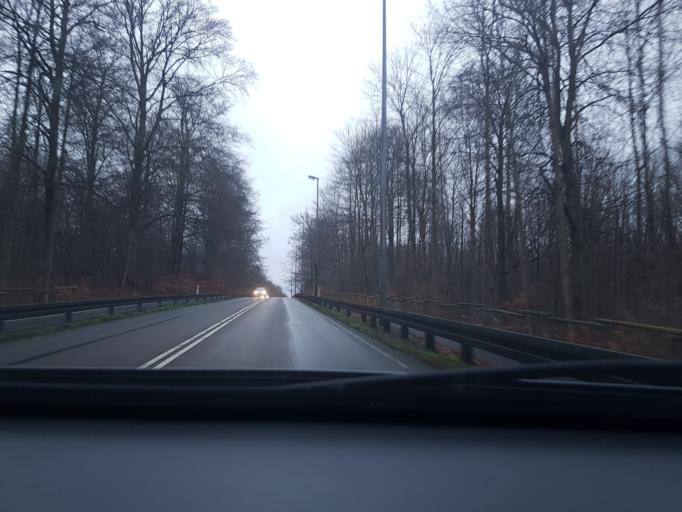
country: DK
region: Capital Region
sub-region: Fureso Kommune
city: Vaerlose
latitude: 55.7578
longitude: 12.3710
